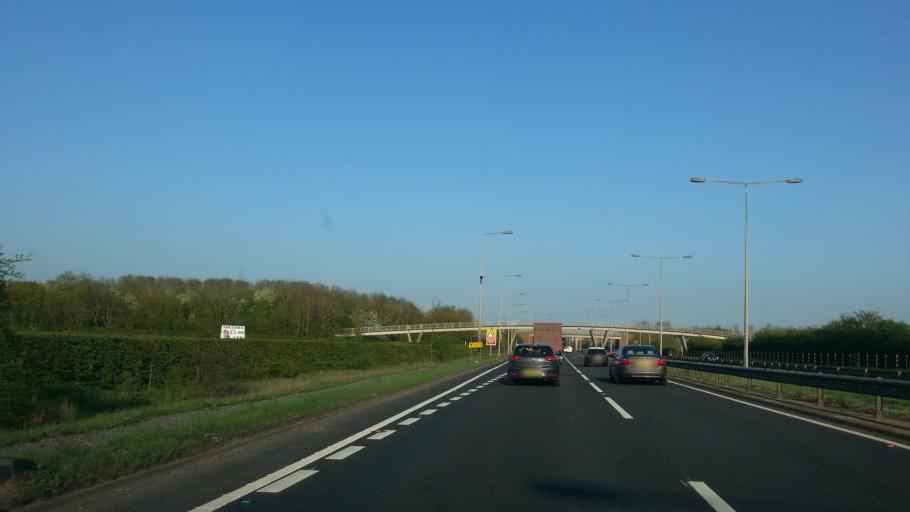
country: GB
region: England
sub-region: Northamptonshire
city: Earls Barton
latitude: 52.2549
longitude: -0.7629
